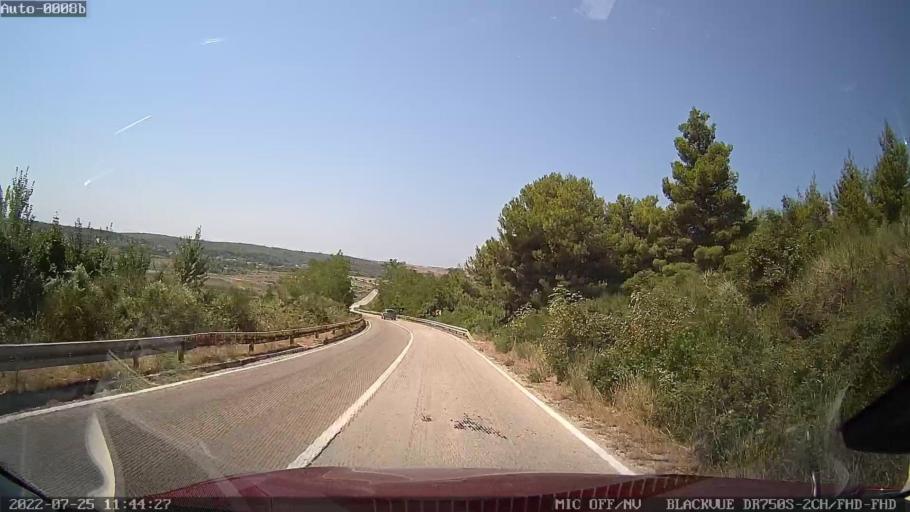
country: HR
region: Zadarska
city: Razanac
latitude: 44.2580
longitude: 15.3225
